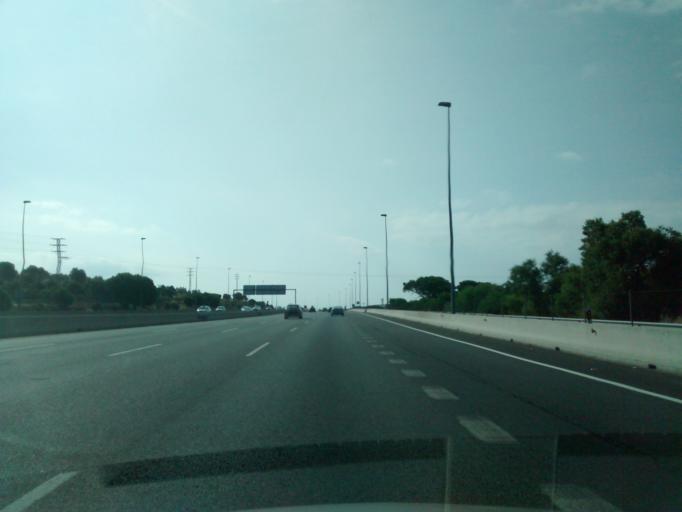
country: ES
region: Madrid
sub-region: Provincia de Madrid
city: Collado-Villalba
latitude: 40.6097
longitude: -3.9754
